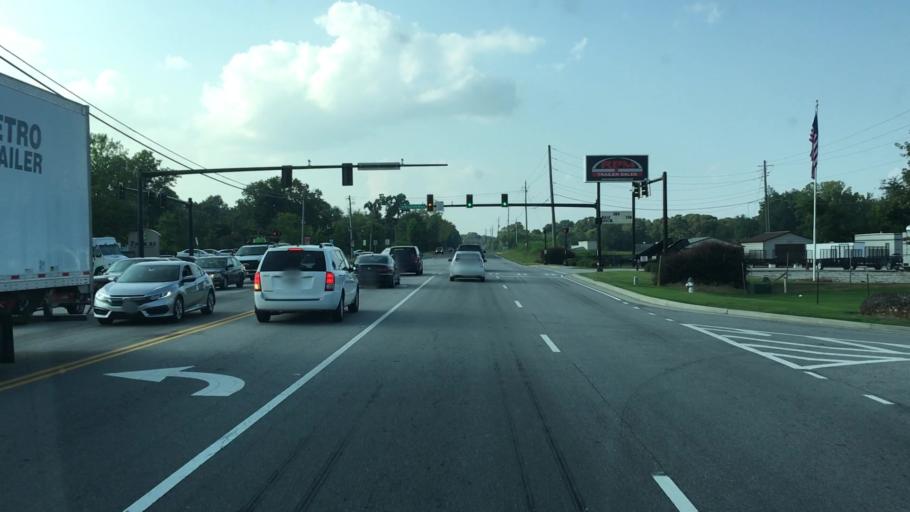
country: US
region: Georgia
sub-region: Jackson County
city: Braselton
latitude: 34.1223
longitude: -83.7636
